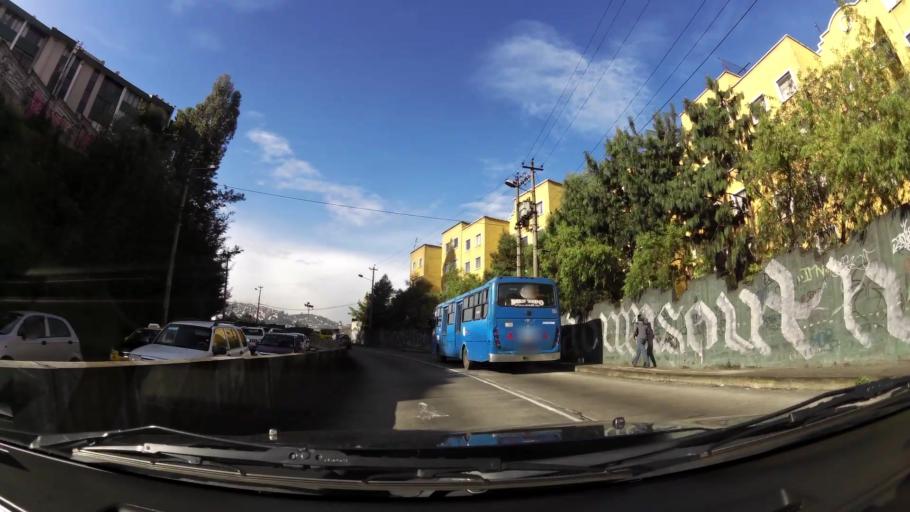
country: EC
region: Pichincha
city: Quito
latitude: -0.2356
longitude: -78.5108
